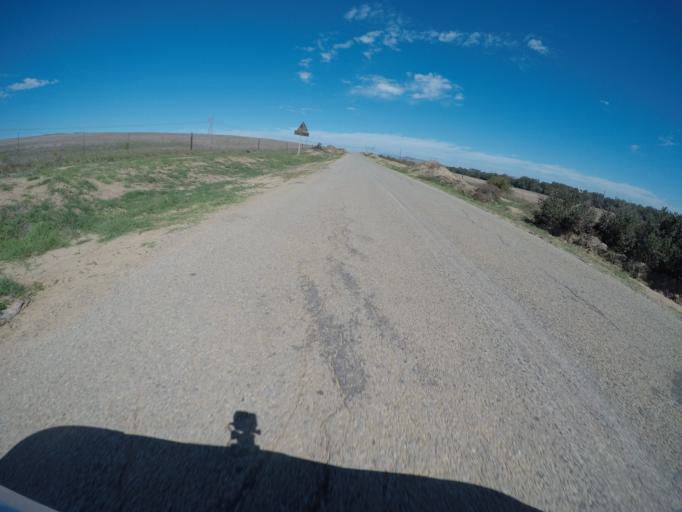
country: ZA
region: Western Cape
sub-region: West Coast District Municipality
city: Malmesbury
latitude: -33.5922
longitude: 18.6451
